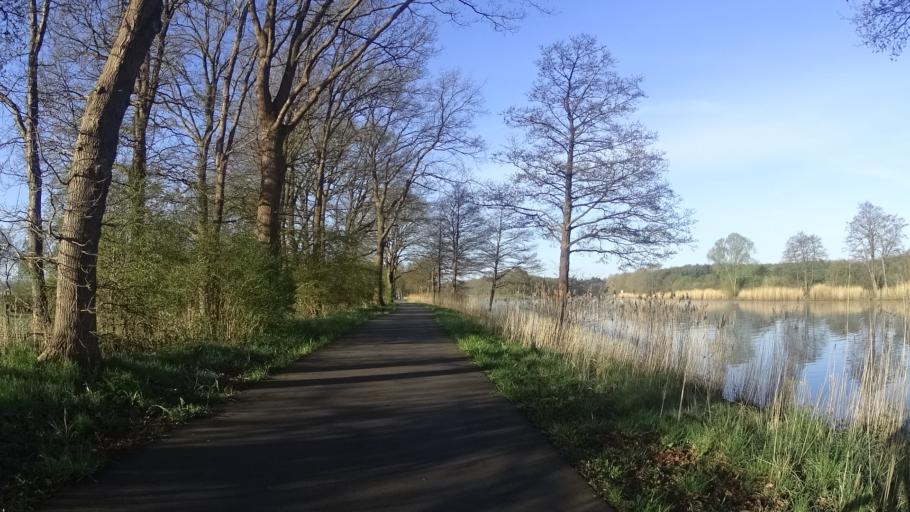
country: DE
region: Lower Saxony
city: Niederlangen
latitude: 52.8396
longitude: 7.2861
